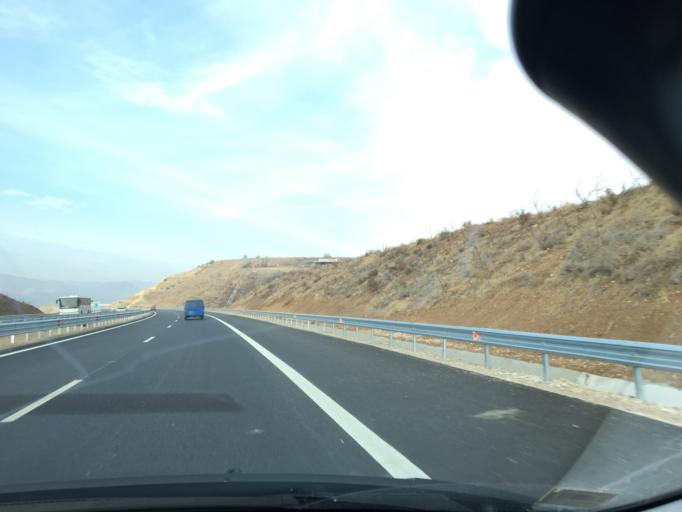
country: BG
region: Blagoevgrad
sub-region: Obshtina Sandanski
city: Sandanski
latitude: 41.5246
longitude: 23.2688
